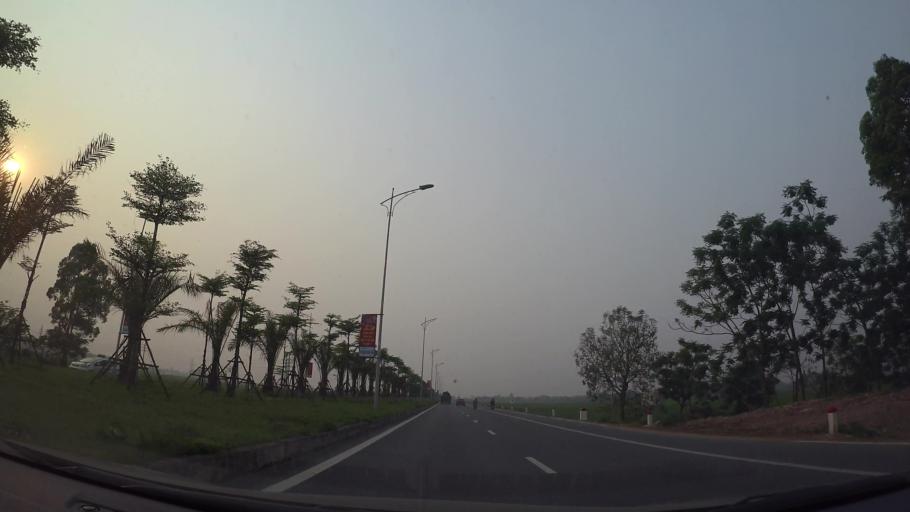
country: VN
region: Ha Noi
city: Kim Bai
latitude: 20.8834
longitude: 105.7983
